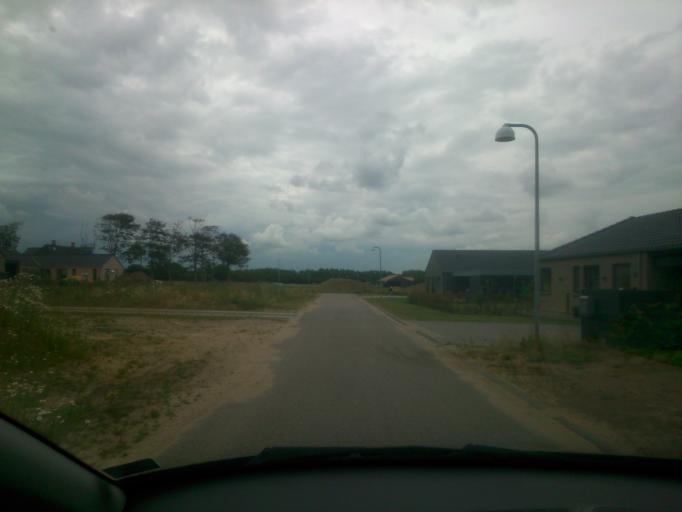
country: DK
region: South Denmark
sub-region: Esbjerg Kommune
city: Esbjerg
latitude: 55.5271
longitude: 8.4300
